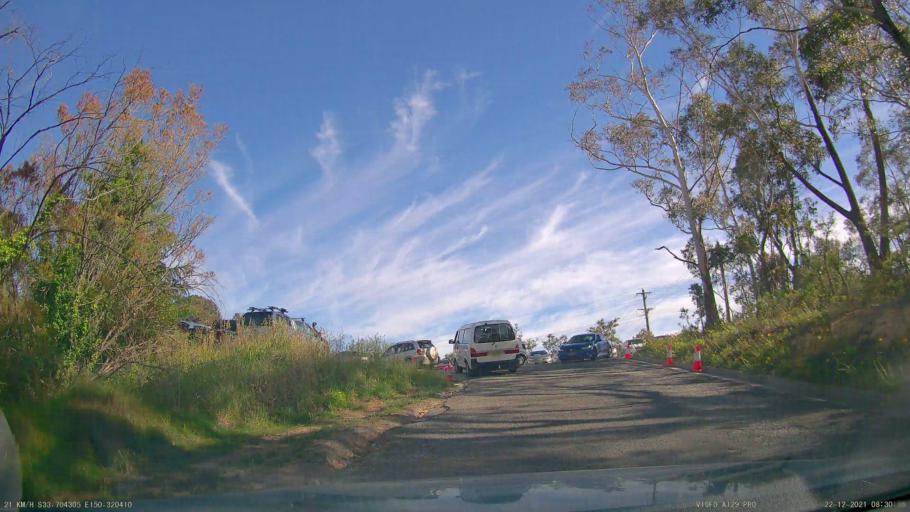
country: AU
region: New South Wales
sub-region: Blue Mountains Municipality
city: Leura
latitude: -33.7042
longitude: 150.3204
